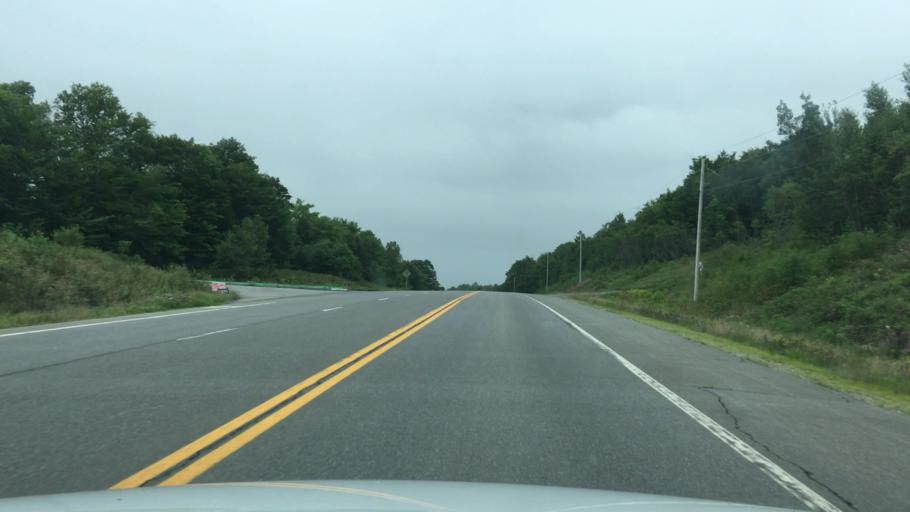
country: US
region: Maine
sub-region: Hancock County
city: Franklin
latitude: 44.8277
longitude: -68.1224
